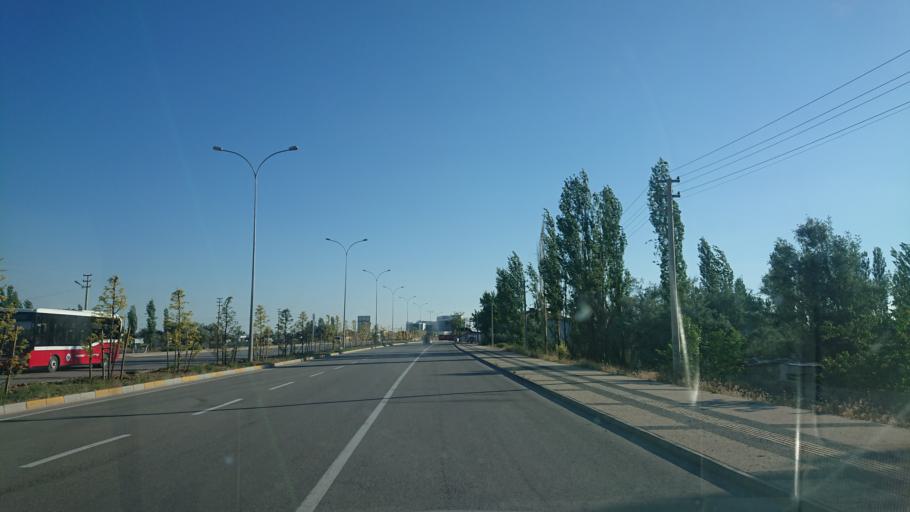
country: TR
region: Aksaray
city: Aksaray
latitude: 38.3817
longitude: 33.9915
